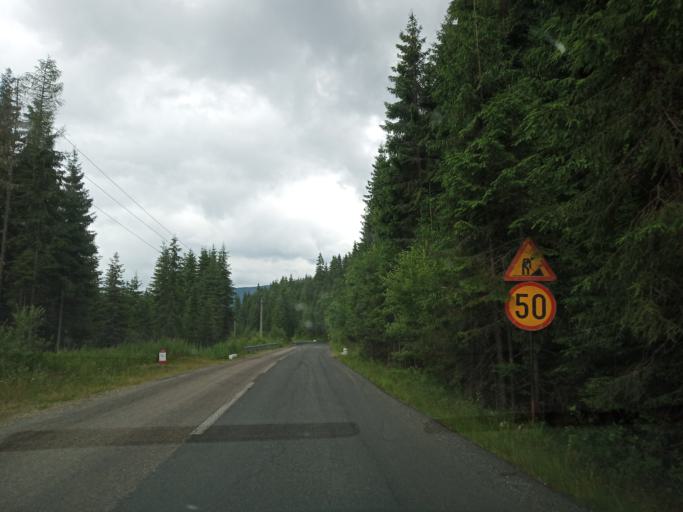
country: RO
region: Gorj
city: Novaci-Straini
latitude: 45.4249
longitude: 23.6894
